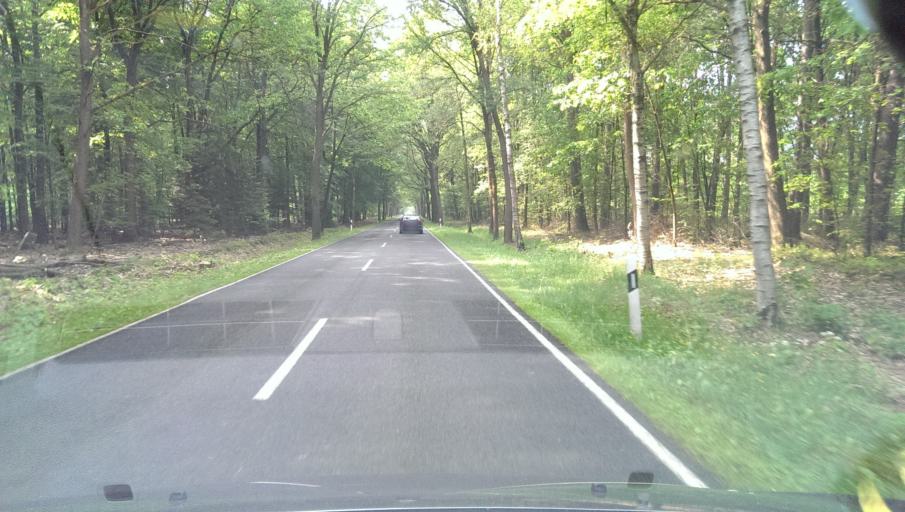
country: DE
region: Lower Saxony
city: Sprakensehl
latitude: 52.7808
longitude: 10.4229
